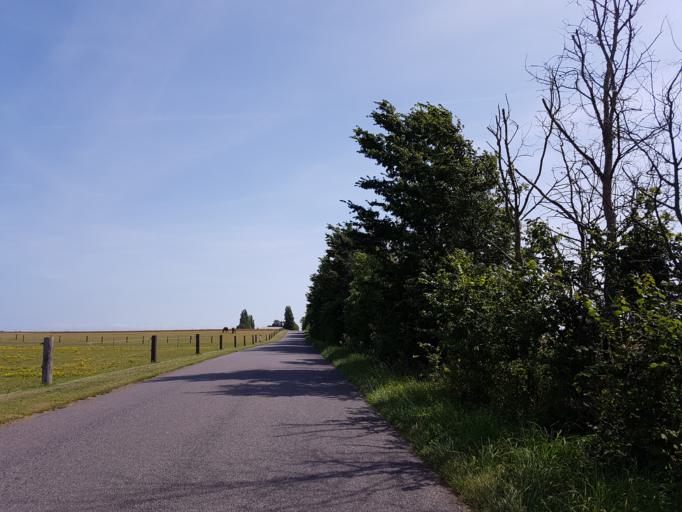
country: DK
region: Zealand
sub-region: Guldborgsund Kommune
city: Nykobing Falster
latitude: 54.5855
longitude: 11.9408
